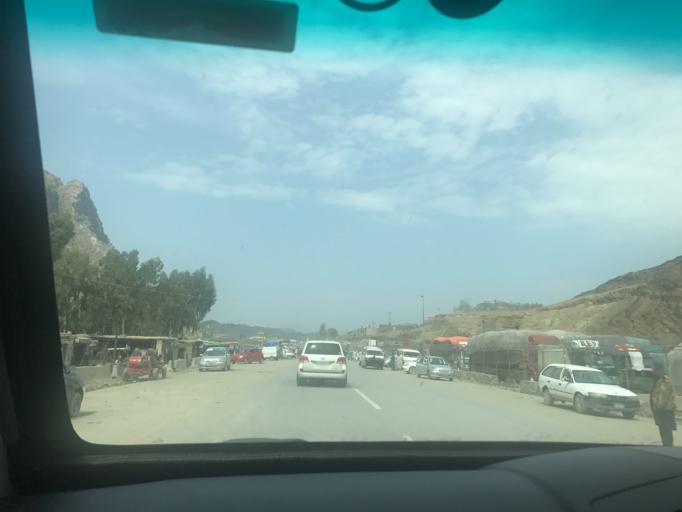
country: PK
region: Federally Administered Tribal Areas
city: Landi Kotal
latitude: 34.1178
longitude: 71.1003
